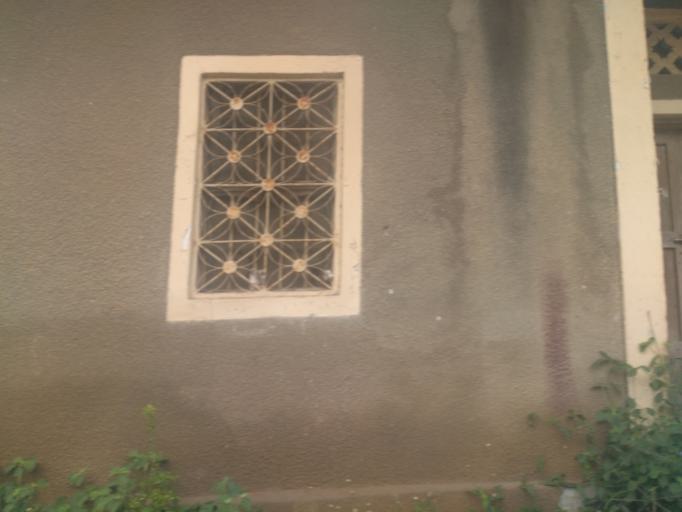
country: TZ
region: Zanzibar Urban/West
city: Zanzibar
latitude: -6.1635
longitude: 39.1982
